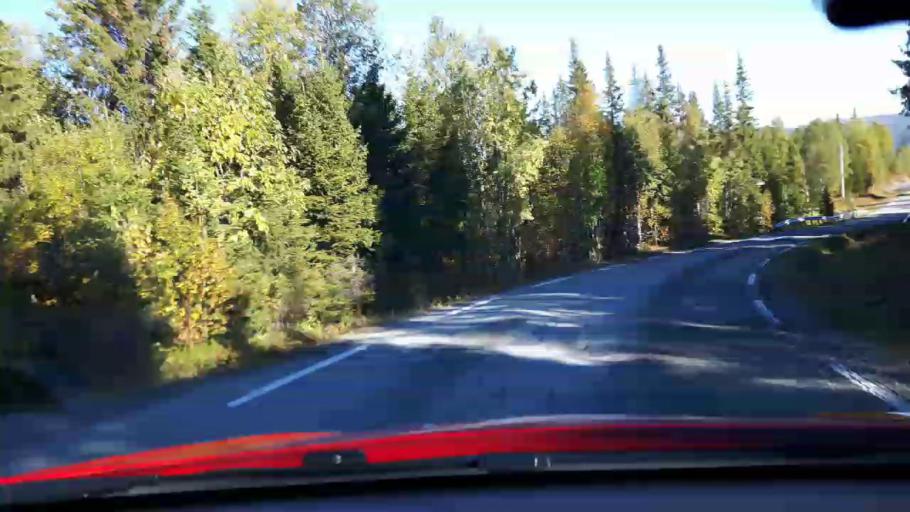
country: NO
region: Nord-Trondelag
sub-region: Lierne
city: Sandvika
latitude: 64.6261
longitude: 13.6845
